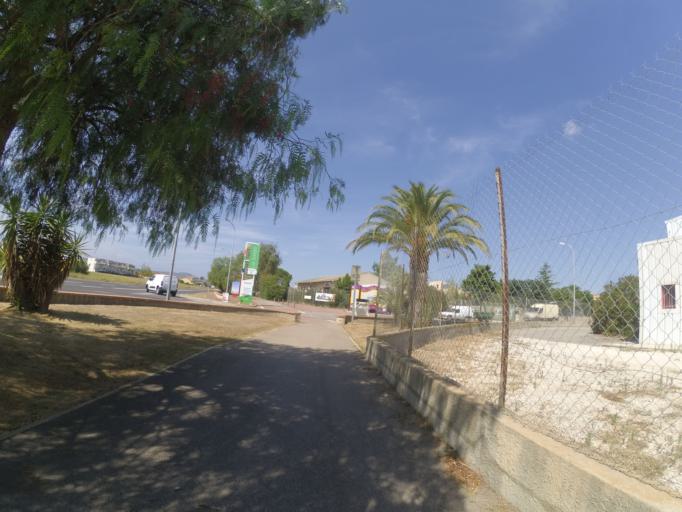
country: FR
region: Languedoc-Roussillon
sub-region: Departement des Pyrenees-Orientales
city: Rivesaltes
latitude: 42.7799
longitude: 2.8785
